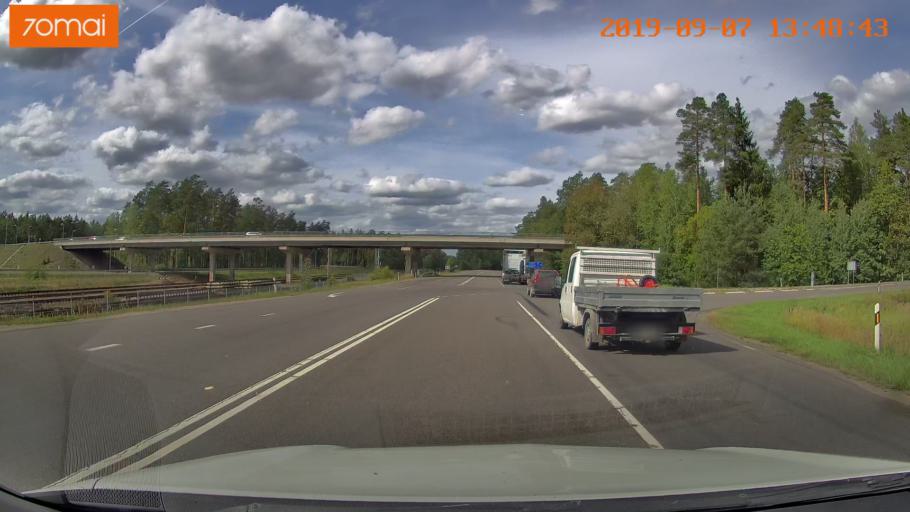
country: LT
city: Baltoji Voke
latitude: 54.6031
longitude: 25.1992
